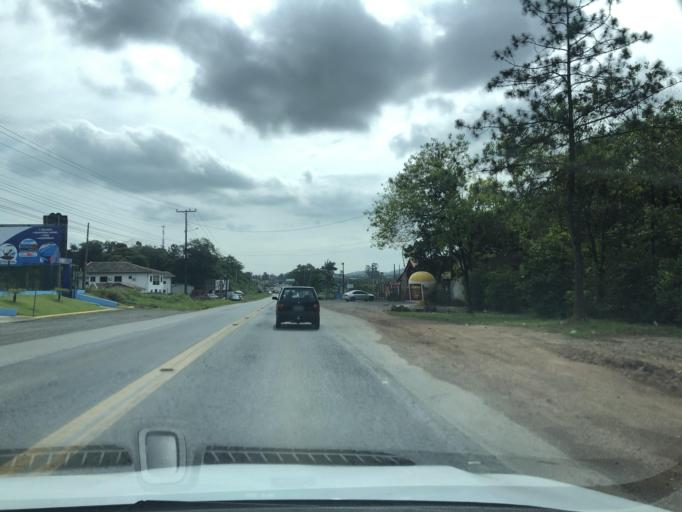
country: BR
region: Santa Catarina
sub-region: Joinville
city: Joinville
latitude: -26.4172
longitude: -48.7744
